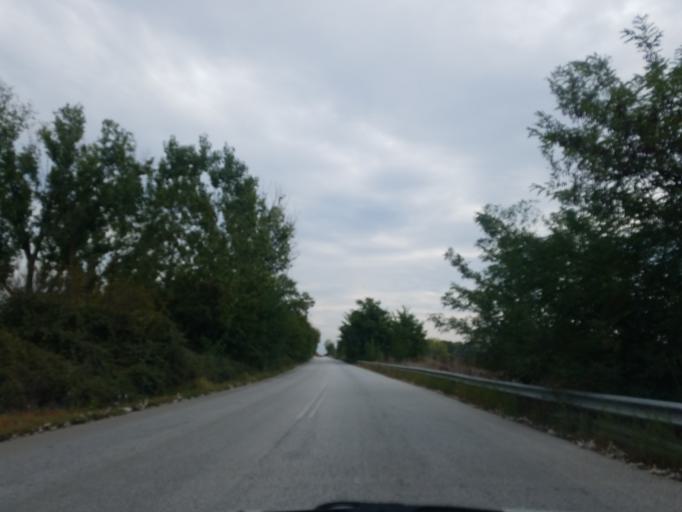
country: GR
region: Thessaly
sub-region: Nomos Kardhitsas
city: Sofades
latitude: 39.3284
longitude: 22.0896
